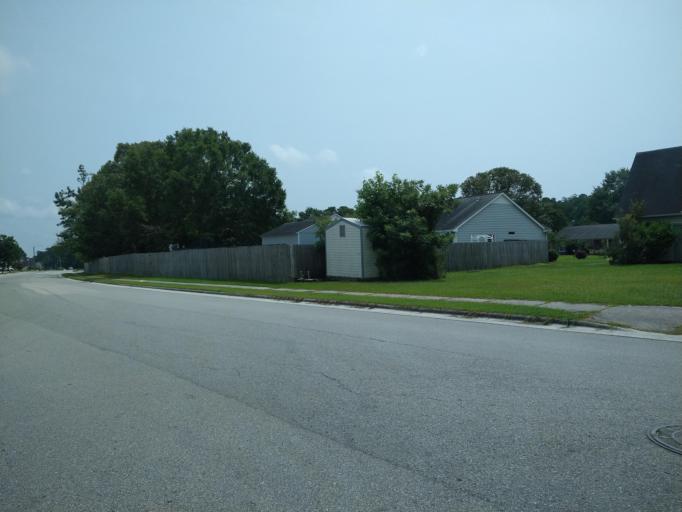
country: US
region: North Carolina
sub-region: Onslow County
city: Pumpkin Center
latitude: 34.7602
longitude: -77.3712
